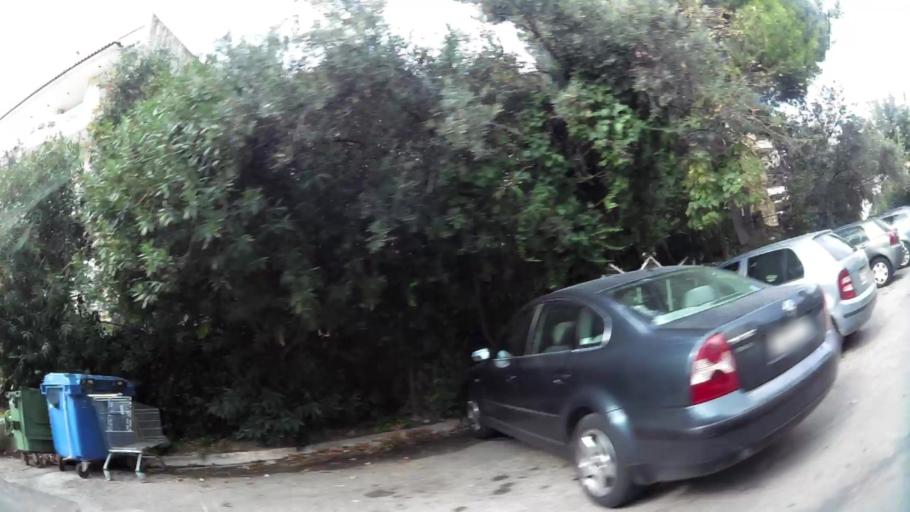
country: GR
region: Attica
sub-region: Nomarchia Athinas
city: Melissia
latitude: 38.0564
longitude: 23.8311
